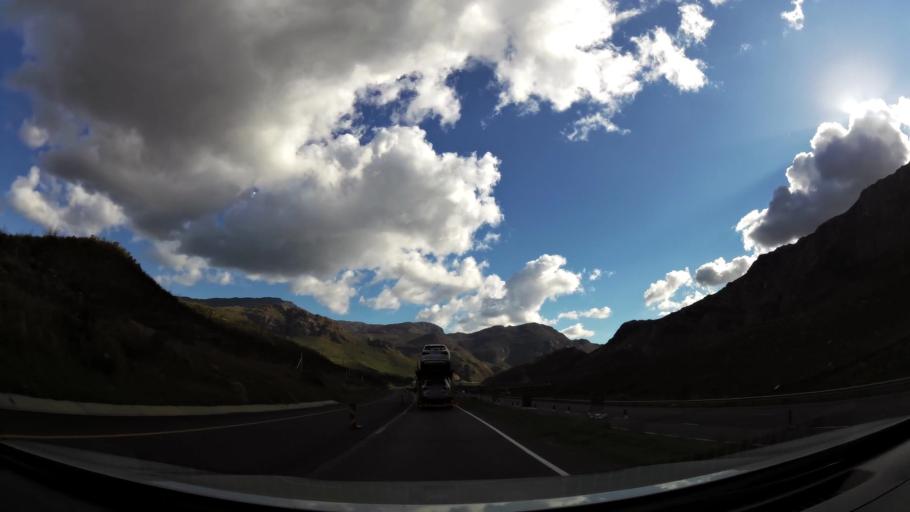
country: ZA
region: Western Cape
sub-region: Cape Winelands District Municipality
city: Paarl
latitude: -33.7256
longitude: 19.1429
